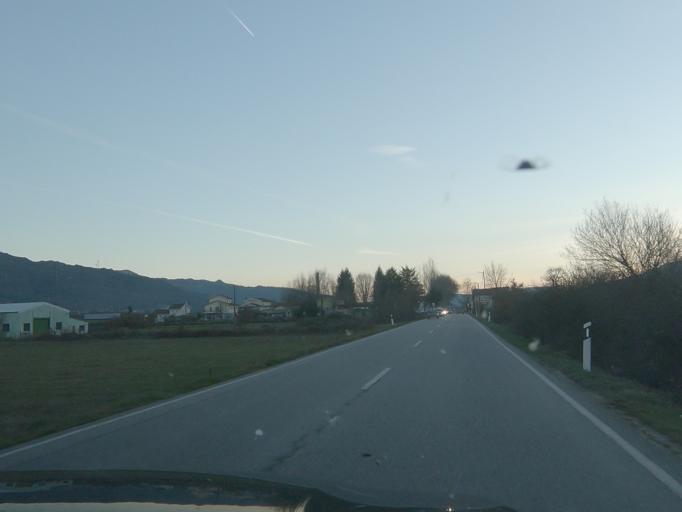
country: PT
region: Vila Real
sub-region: Vila Pouca de Aguiar
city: Vila Pouca de Aguiar
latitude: 41.4529
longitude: -7.6686
